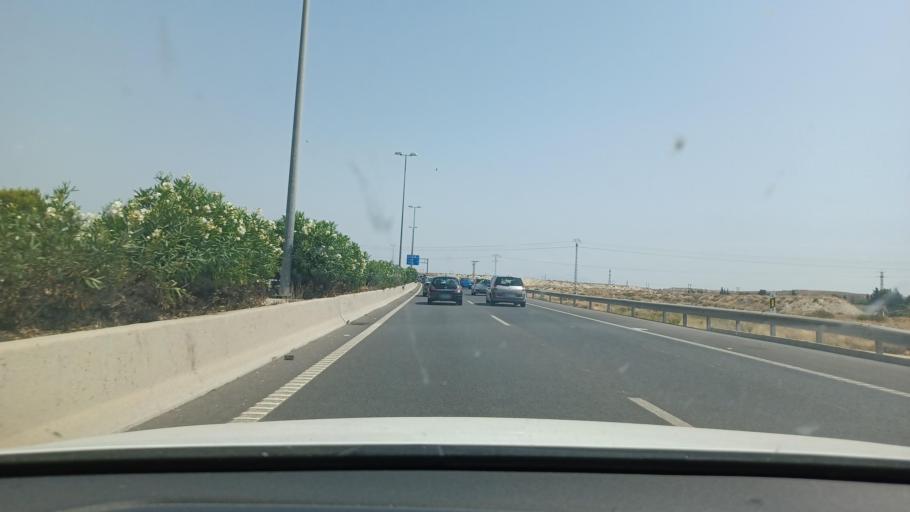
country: ES
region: Valencia
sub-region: Provincia de Alicante
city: San Vicent del Raspeig
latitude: 38.3546
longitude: -0.5400
